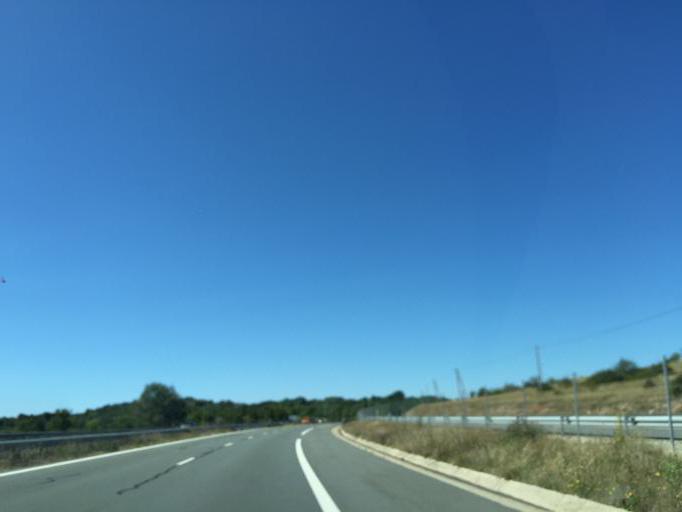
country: FR
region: Midi-Pyrenees
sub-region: Departement de l'Aveyron
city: La Cavalerie
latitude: 43.8908
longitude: 3.2847
